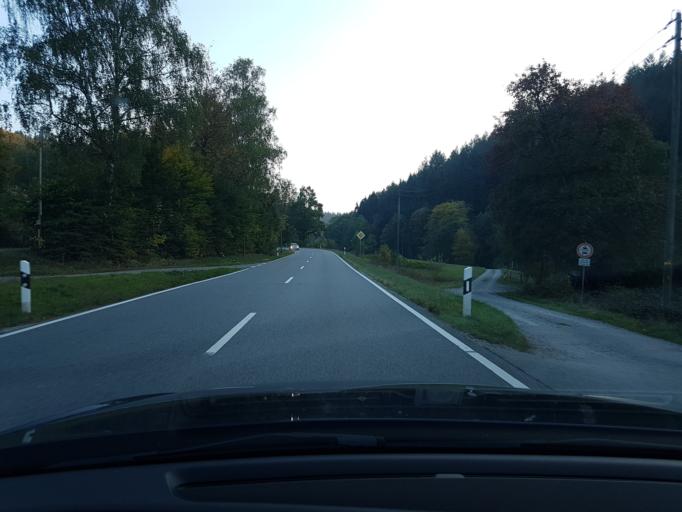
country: DE
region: Hesse
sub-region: Regierungsbezirk Darmstadt
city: Rothenberg
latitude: 49.5132
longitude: 8.9655
